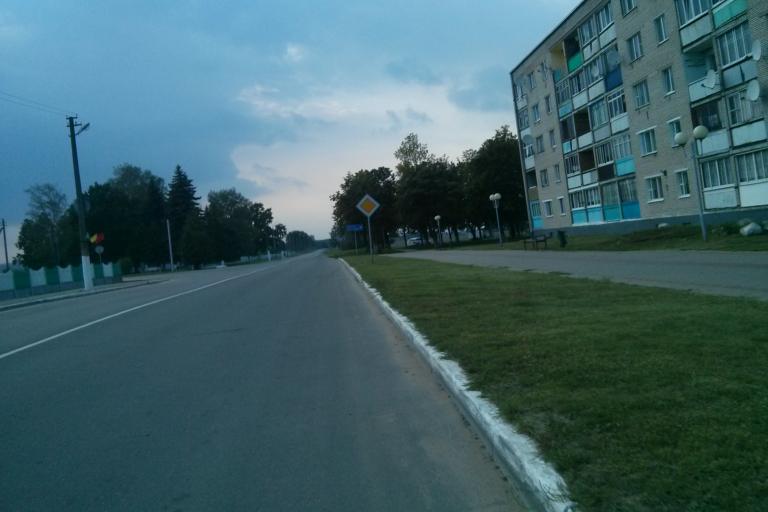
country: BY
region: Minsk
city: Chervyen'
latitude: 53.7193
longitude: 28.3986
